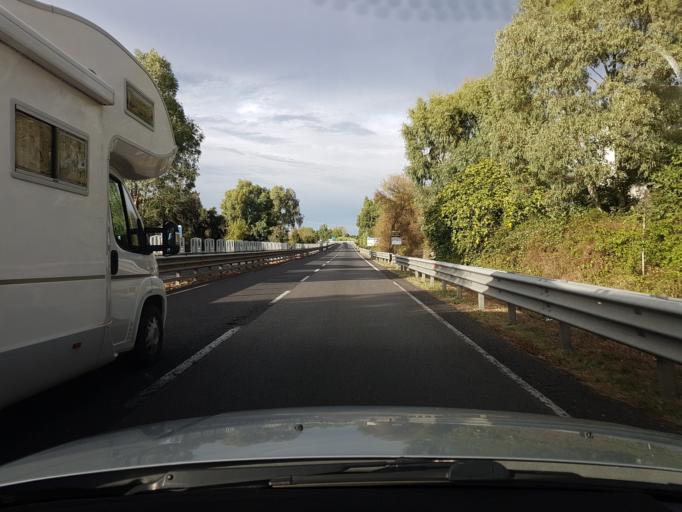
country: IT
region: Sardinia
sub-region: Provincia di Oristano
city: Paulilatino
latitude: 40.1052
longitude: 8.7891
